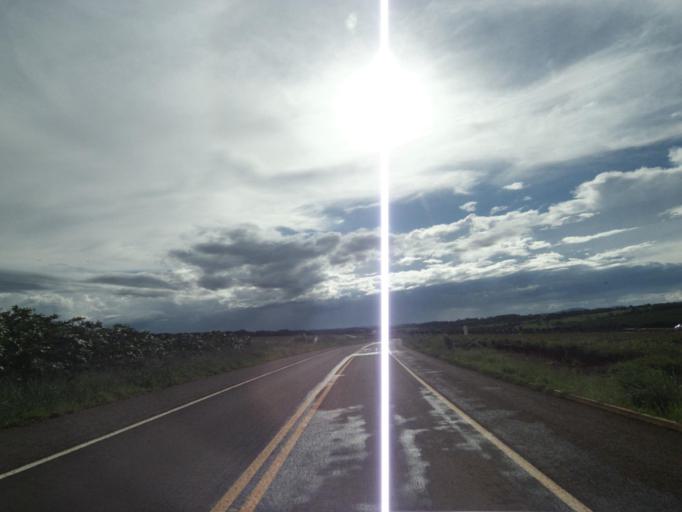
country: BR
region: Goias
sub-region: Jaragua
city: Jaragua
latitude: -15.9017
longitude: -49.5340
